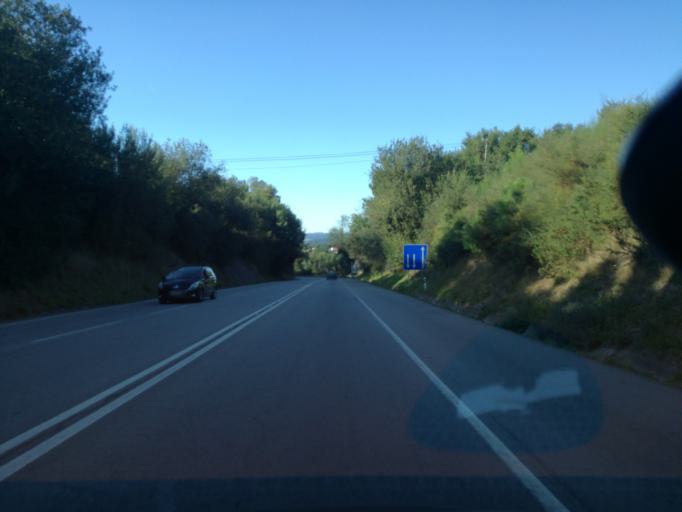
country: PT
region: Porto
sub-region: Santo Tirso
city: Sao Miguel do Couto
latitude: 41.3207
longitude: -8.4691
